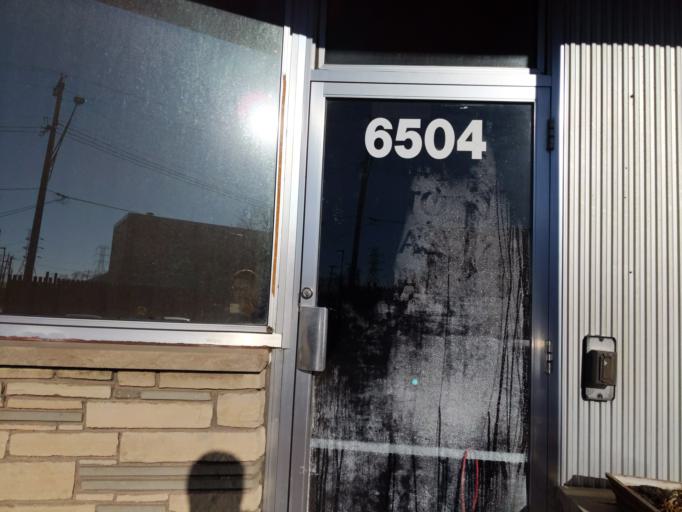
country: US
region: Minnesota
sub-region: Hennepin County
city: Saint Louis Park
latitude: 44.9391
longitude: -93.3622
